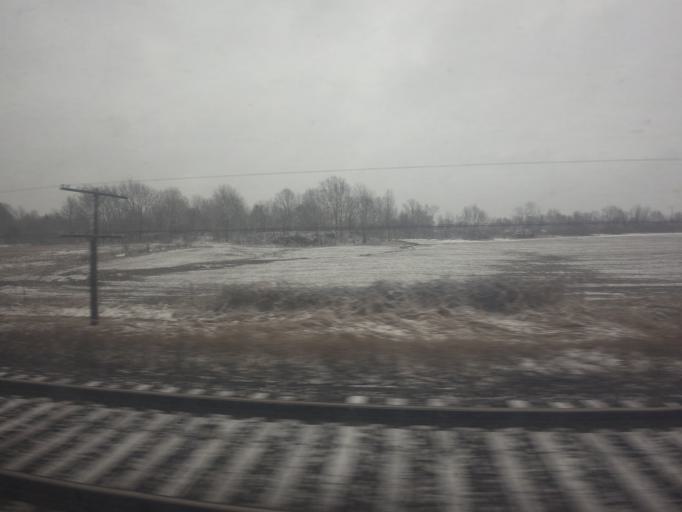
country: US
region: New York
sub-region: Jefferson County
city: Alexandria Bay
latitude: 44.4925
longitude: -75.8712
